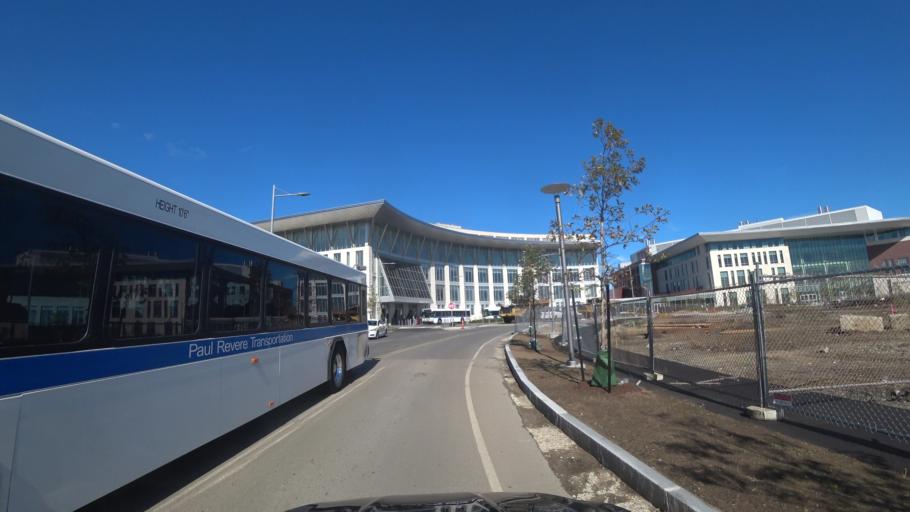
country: US
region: Massachusetts
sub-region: Suffolk County
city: South Boston
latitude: 42.3119
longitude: -71.0367
